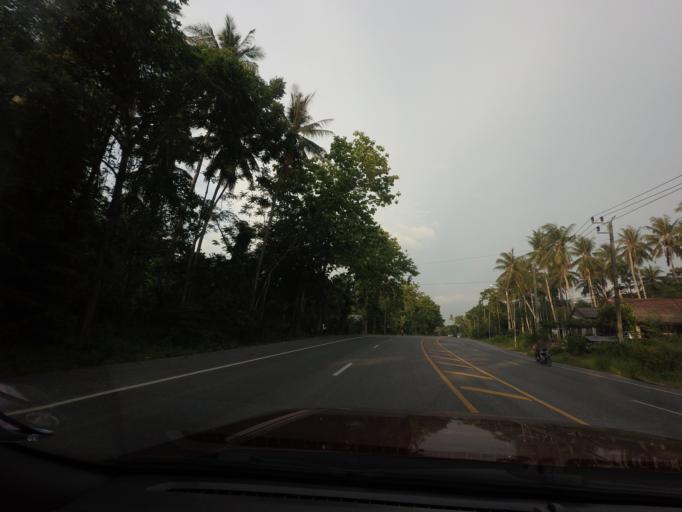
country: TH
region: Pattani
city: Khok Pho
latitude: 6.6771
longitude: 101.1356
